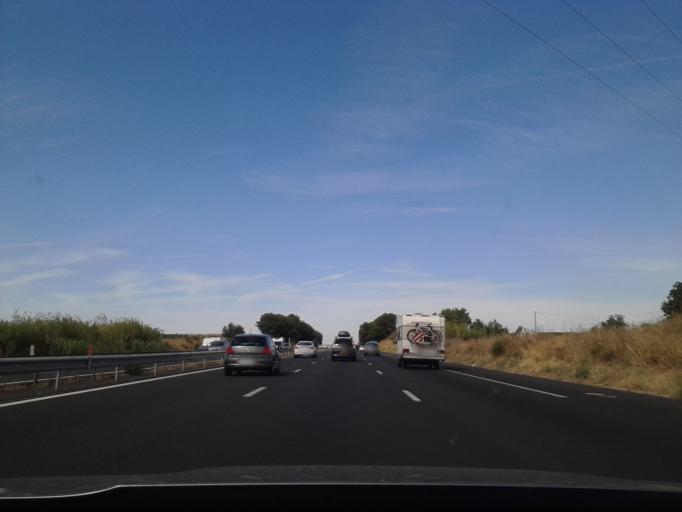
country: FR
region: Languedoc-Roussillon
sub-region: Departement de l'Herault
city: Pinet
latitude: 43.4084
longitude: 3.4978
